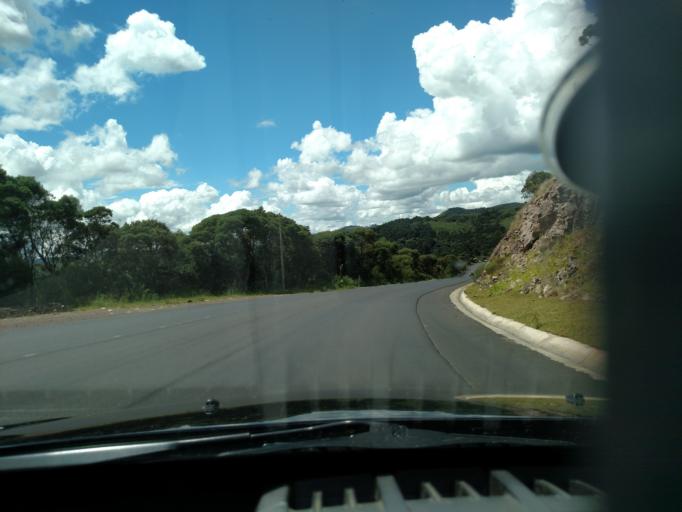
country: BR
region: Santa Catarina
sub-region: Sao Joaquim
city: Sao Joaquim
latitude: -28.2797
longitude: -49.9609
